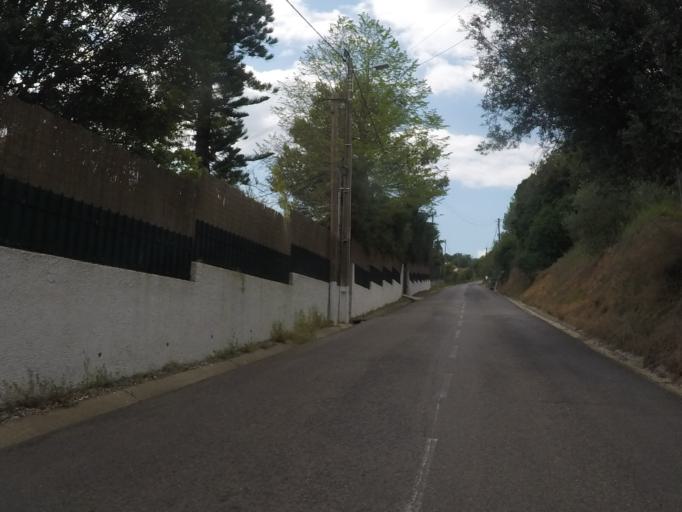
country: PT
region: Setubal
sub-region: Palmela
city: Quinta do Anjo
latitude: 38.5093
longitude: -9.0028
